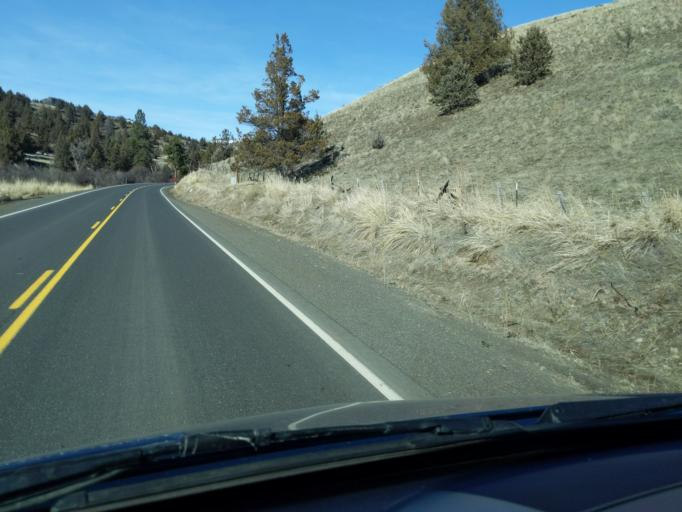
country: US
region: Oregon
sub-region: Grant County
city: John Day
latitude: 44.8427
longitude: -119.0317
